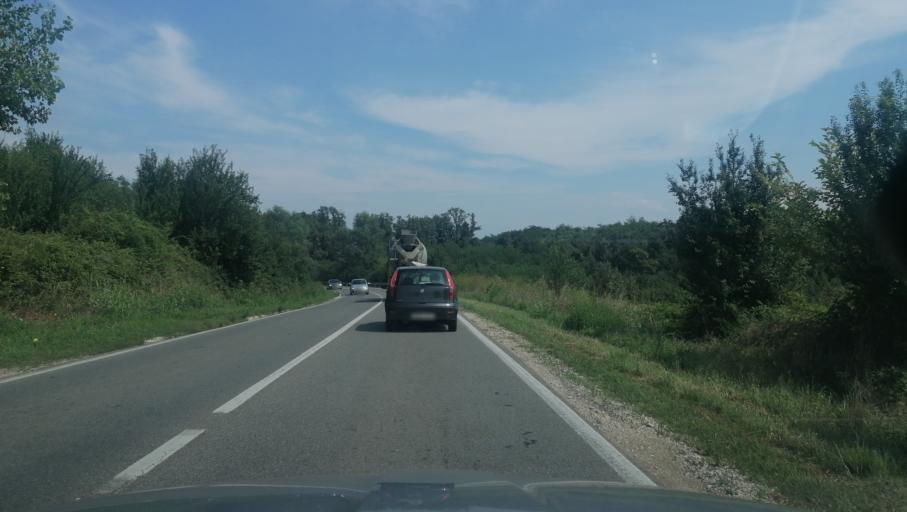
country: BA
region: Republika Srpska
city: Velika Obarska
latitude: 44.7693
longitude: 19.1530
